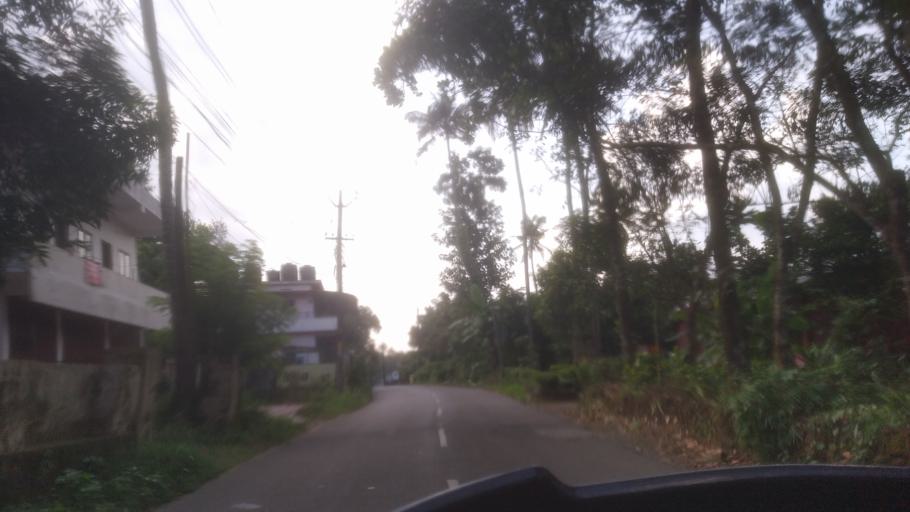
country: IN
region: Kerala
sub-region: Ernakulam
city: Kotamangalam
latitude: 10.0067
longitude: 76.6746
